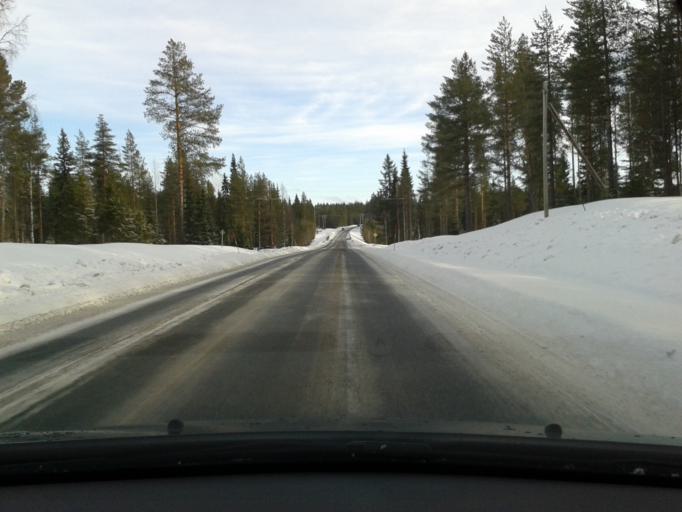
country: SE
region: Vaesterbotten
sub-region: Vilhelmina Kommun
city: Vilhelmina
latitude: 64.6470
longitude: 16.5343
